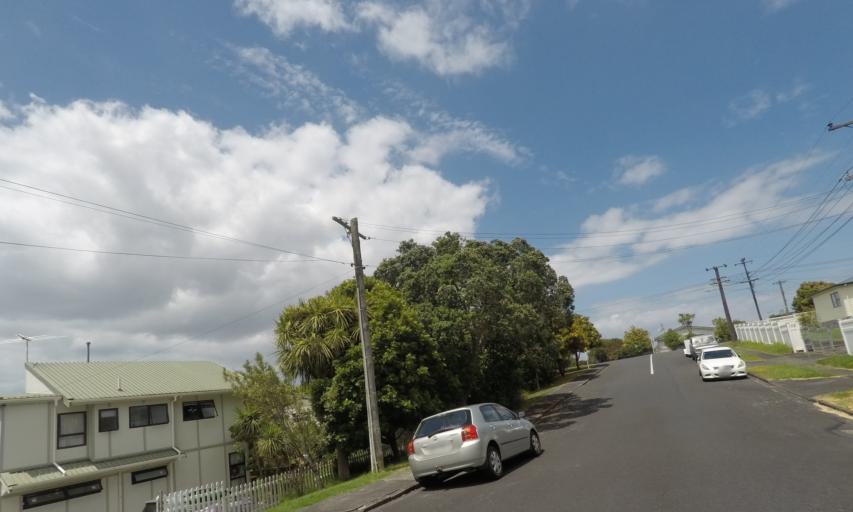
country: NZ
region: Auckland
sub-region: Auckland
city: Waitakere
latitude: -36.9048
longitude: 174.6687
